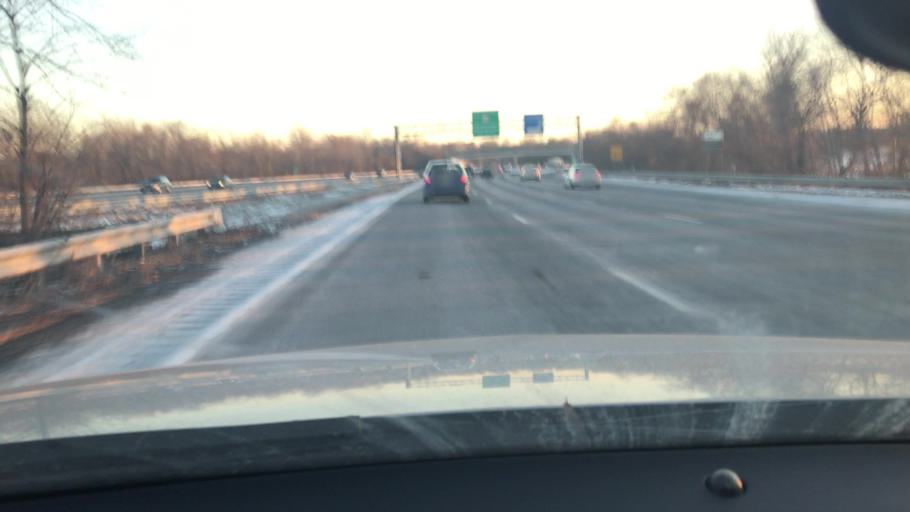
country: US
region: New Jersey
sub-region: Burlington County
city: Bordentown
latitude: 40.1594
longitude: -74.7185
